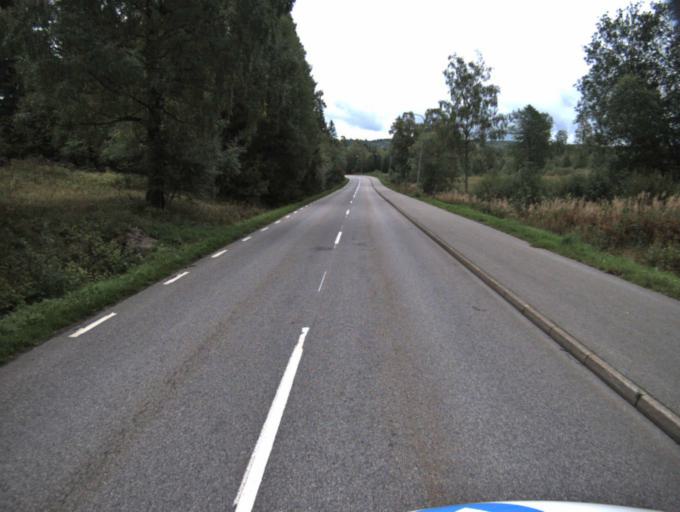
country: SE
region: Vaestra Goetaland
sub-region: Ulricehamns Kommun
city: Ulricehamn
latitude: 57.7706
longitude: 13.4438
